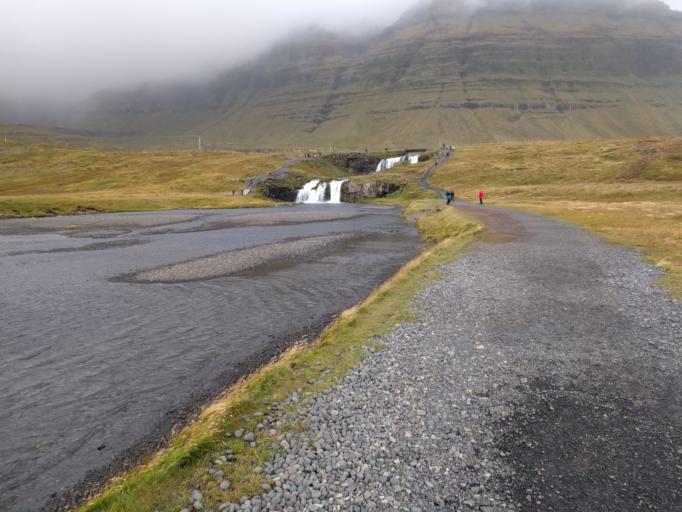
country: IS
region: West
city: Olafsvik
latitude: 64.9271
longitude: -23.3087
